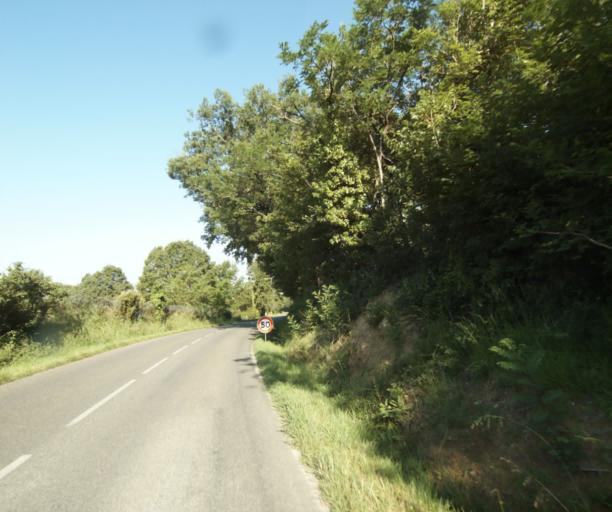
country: FR
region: Midi-Pyrenees
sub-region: Departement du Tarn-et-Garonne
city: Montauban
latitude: 44.0151
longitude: 1.3929
